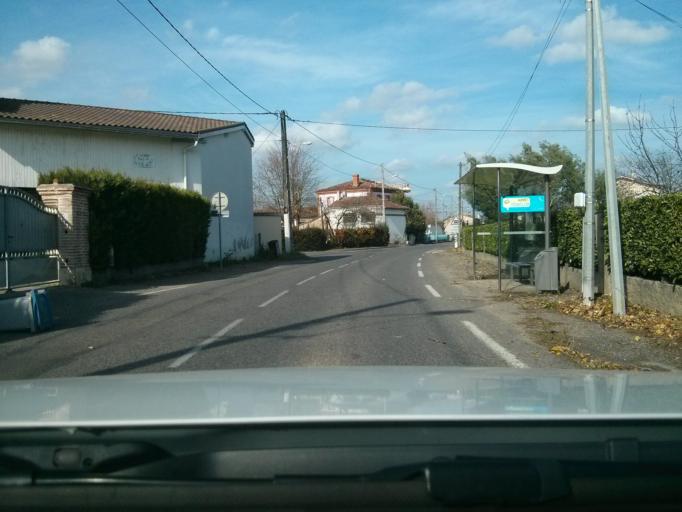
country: FR
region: Midi-Pyrenees
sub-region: Departement du Tarn-et-Garonne
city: Montbeton
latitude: 44.0145
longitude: 1.3216
